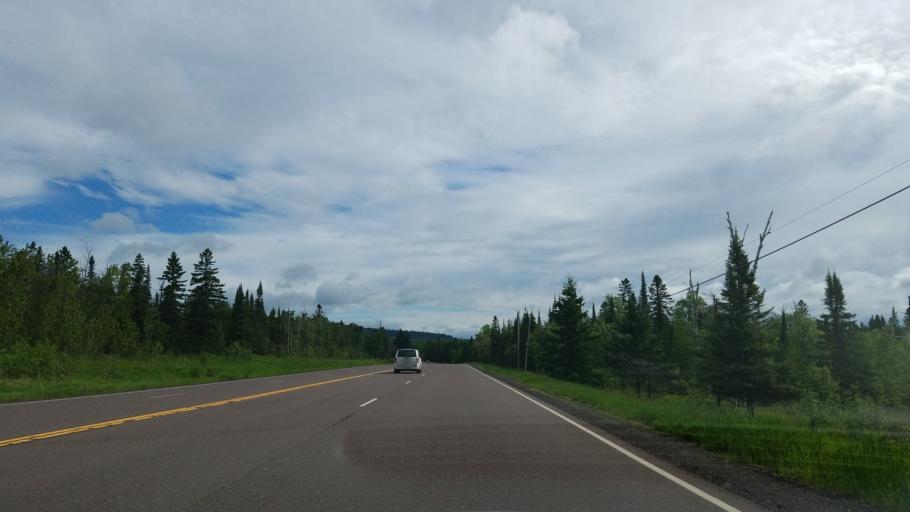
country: US
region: Minnesota
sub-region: Lake County
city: Two Harbors
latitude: 47.0808
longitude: -91.5845
